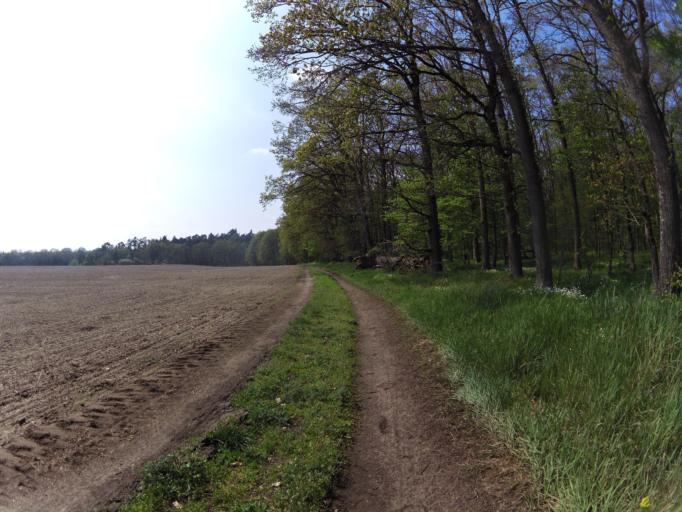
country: DE
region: Bavaria
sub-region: Regierungsbezirk Unterfranken
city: Sommerhausen
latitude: 49.7047
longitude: 10.0592
